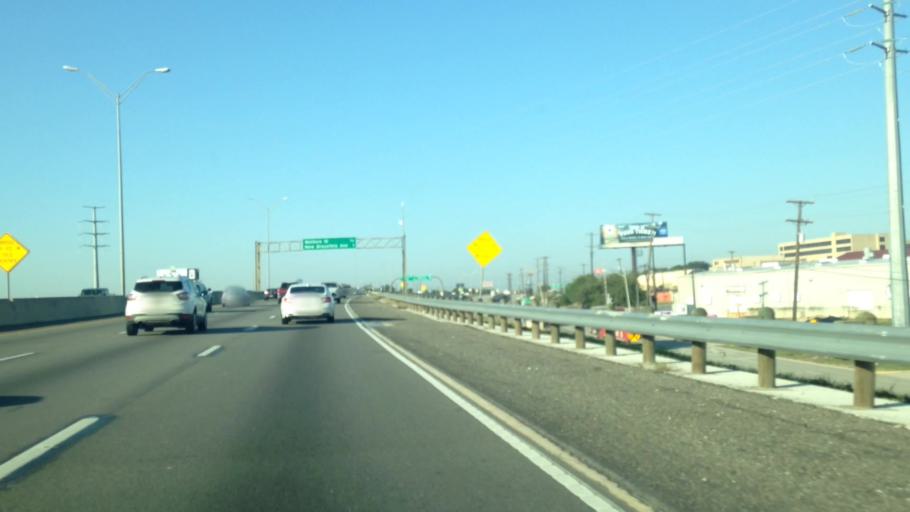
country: US
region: Texas
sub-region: Bexar County
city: Terrell Hills
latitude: 29.4413
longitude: -98.4394
